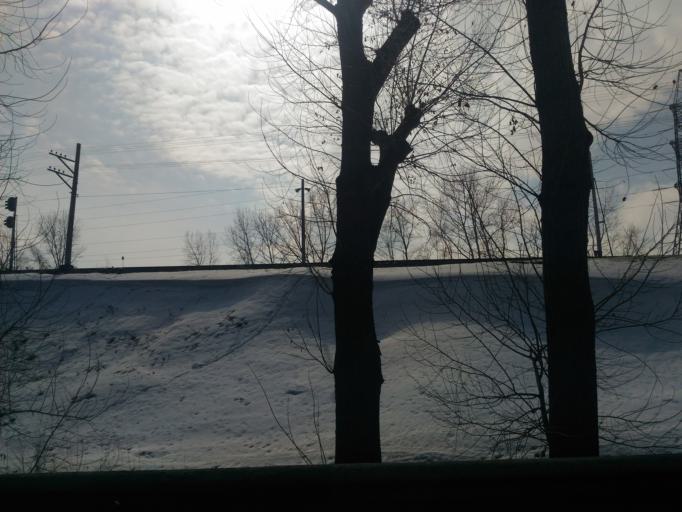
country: RU
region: Ulyanovsk
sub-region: Ulyanovskiy Rayon
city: Ulyanovsk
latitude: 54.3195
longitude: 48.4688
